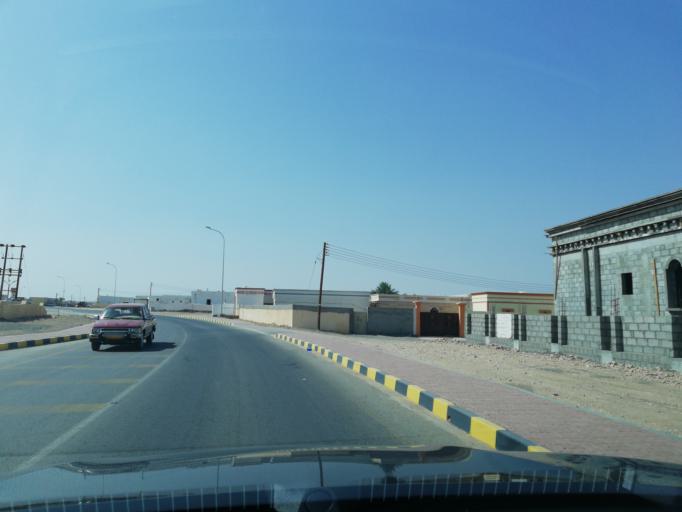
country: OM
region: Muhafazat ad Dakhiliyah
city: Adam
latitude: 22.3012
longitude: 58.0730
